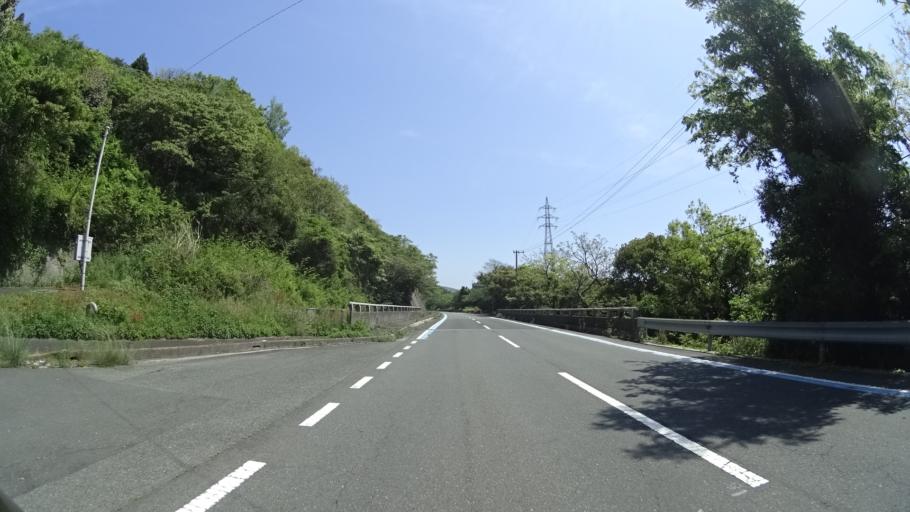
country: JP
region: Ehime
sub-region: Nishiuwa-gun
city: Ikata-cho
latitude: 33.4215
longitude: 132.2041
